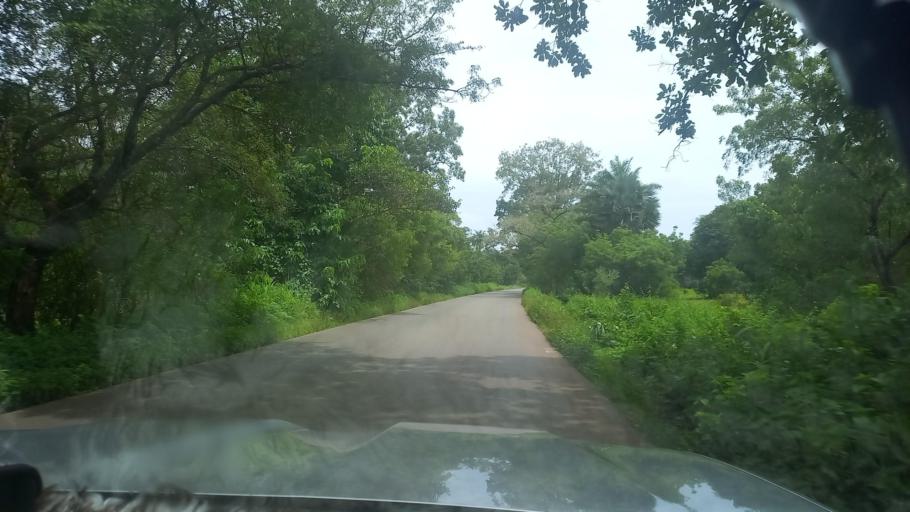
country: SN
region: Kolda
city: Marsassoum
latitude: 12.9586
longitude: -16.0006
